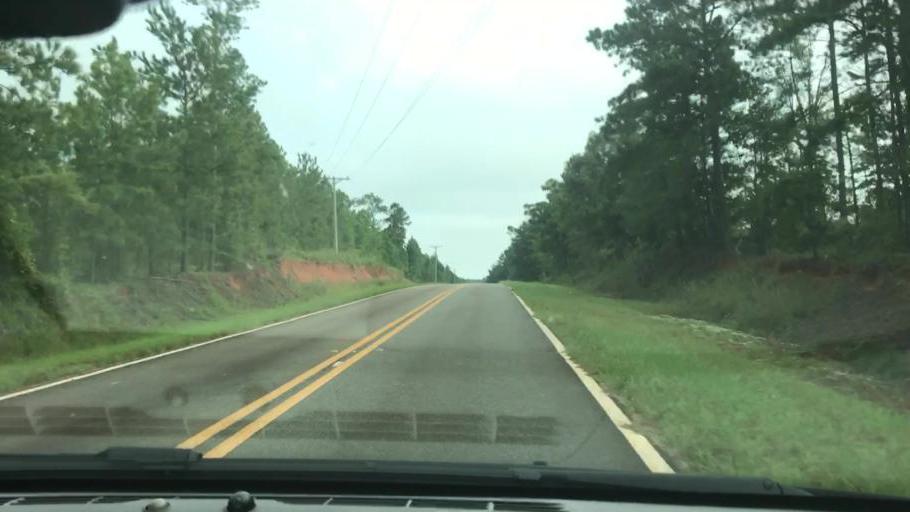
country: US
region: Georgia
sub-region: Stewart County
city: Lumpkin
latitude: 32.0300
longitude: -84.9117
